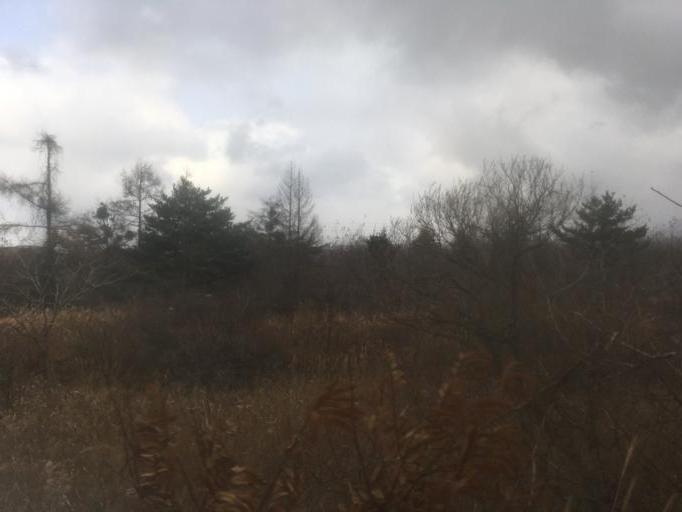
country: JP
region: Aomori
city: Goshogawara
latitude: 41.1804
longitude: 140.4899
